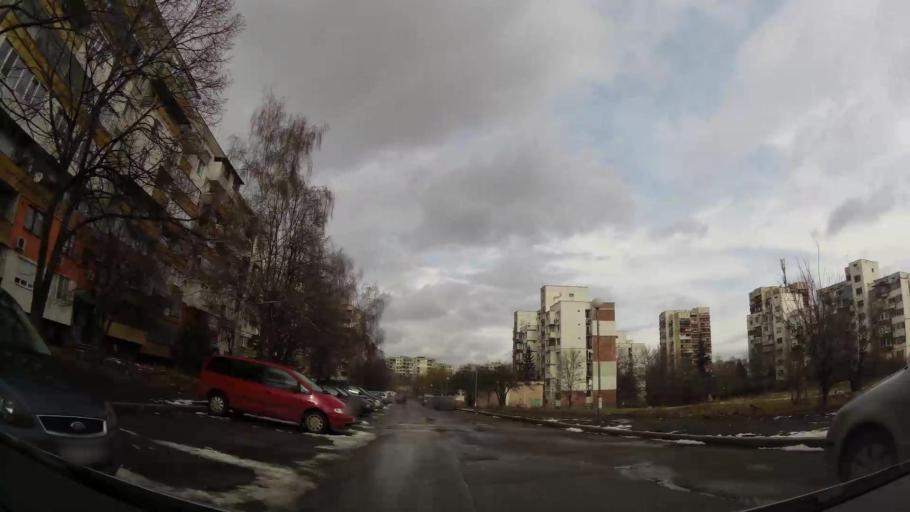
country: BG
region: Sofiya
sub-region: Obshtina Bozhurishte
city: Bozhurishte
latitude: 42.7151
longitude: 23.2409
